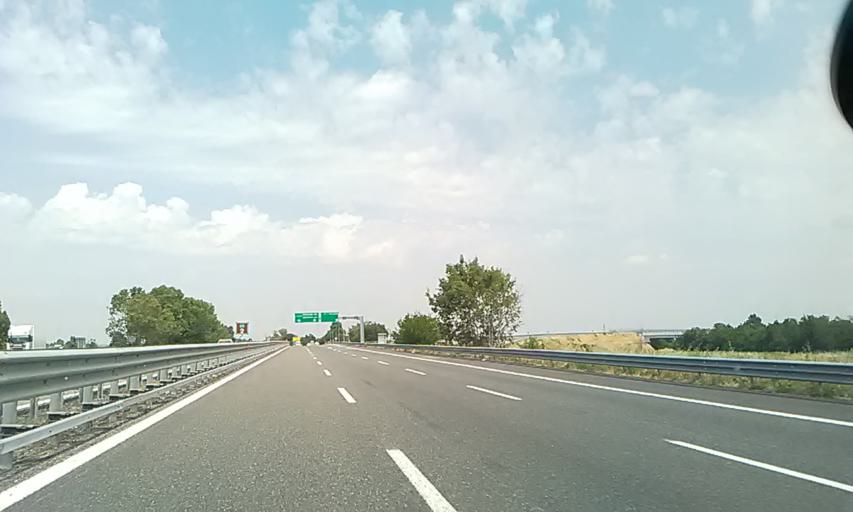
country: IT
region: Piedmont
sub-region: Provincia di Alessandria
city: Predosa
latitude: 44.7540
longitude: 8.6461
